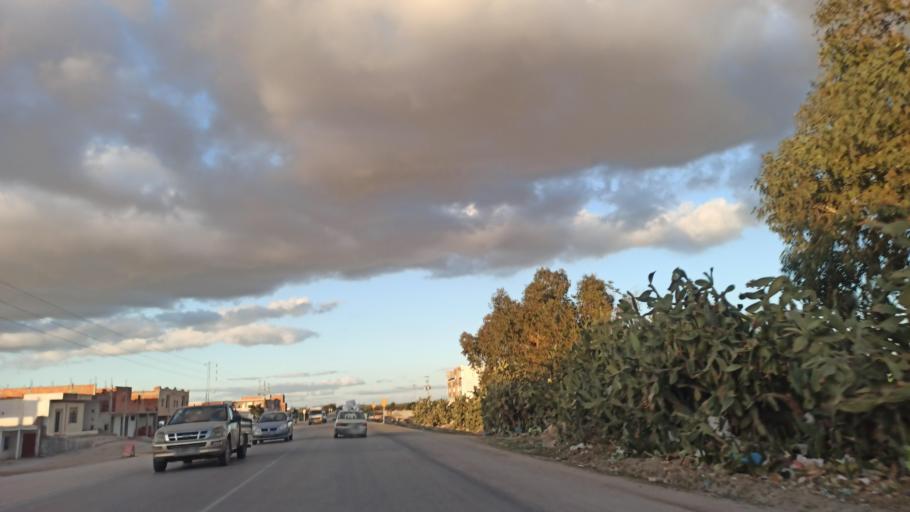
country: TN
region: Susah
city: Sidi Bou Ali
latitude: 36.0099
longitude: 10.3178
